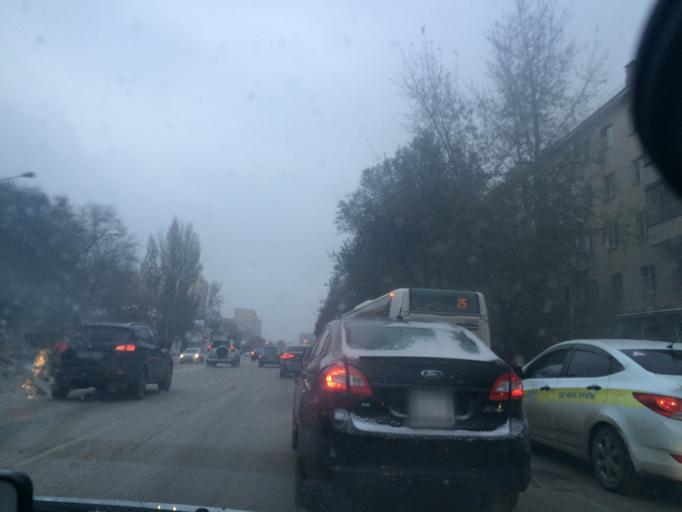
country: KZ
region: Astana Qalasy
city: Astana
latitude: 51.1782
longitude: 71.4103
